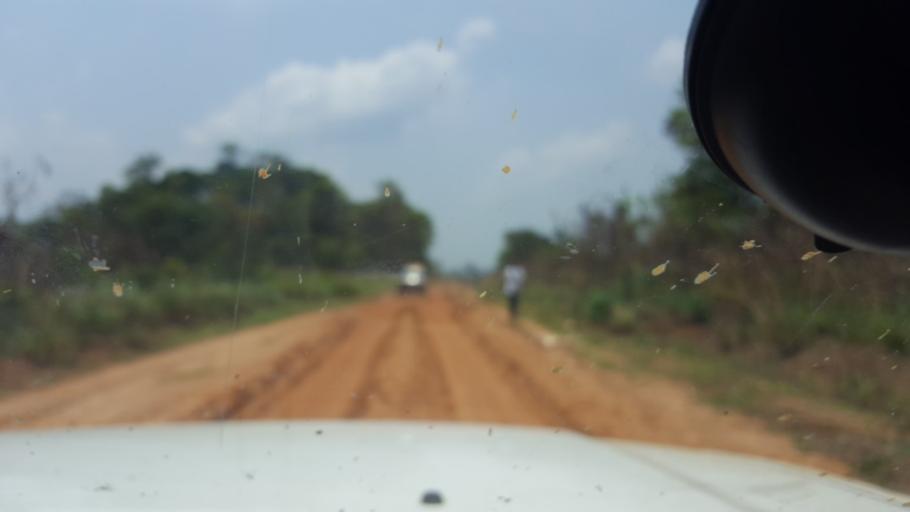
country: CD
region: Bandundu
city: Mushie
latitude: -3.7495
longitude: 16.6316
